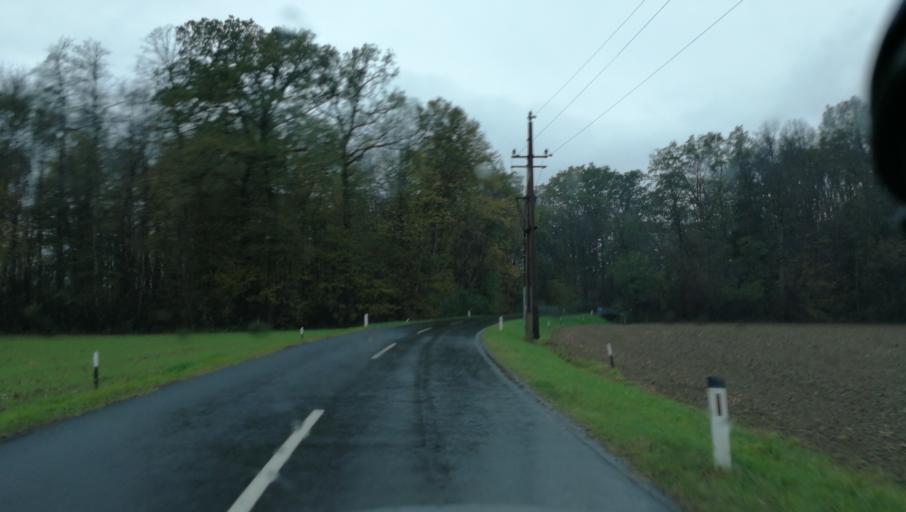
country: AT
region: Styria
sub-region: Politischer Bezirk Leibnitz
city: Spielfeld
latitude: 46.7321
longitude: 15.6738
